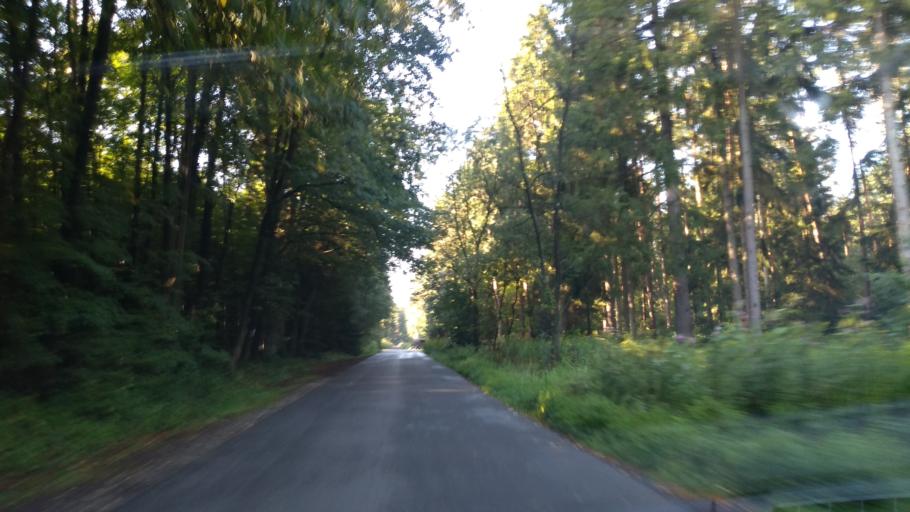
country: DE
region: North Rhine-Westphalia
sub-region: Regierungsbezirk Koln
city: Stossdorf
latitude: 50.8176
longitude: 7.2635
